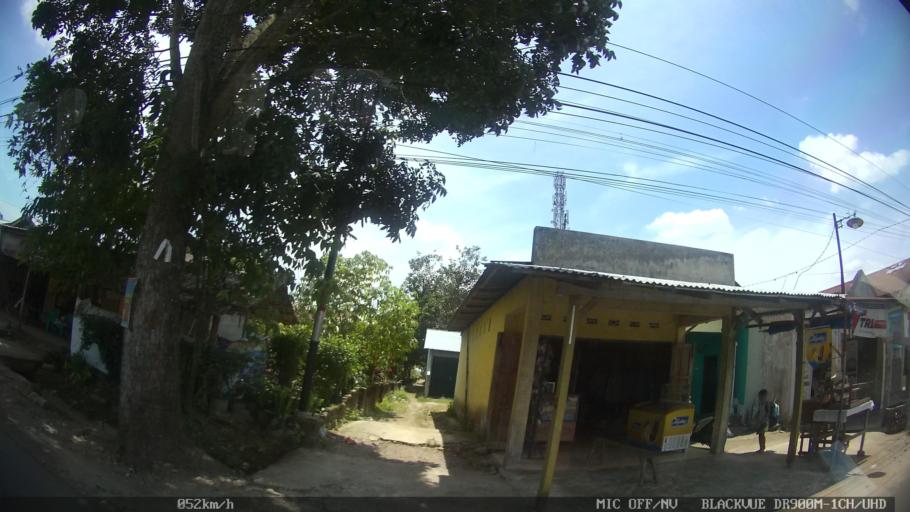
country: ID
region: North Sumatra
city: Binjai
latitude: 3.5961
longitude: 98.5182
